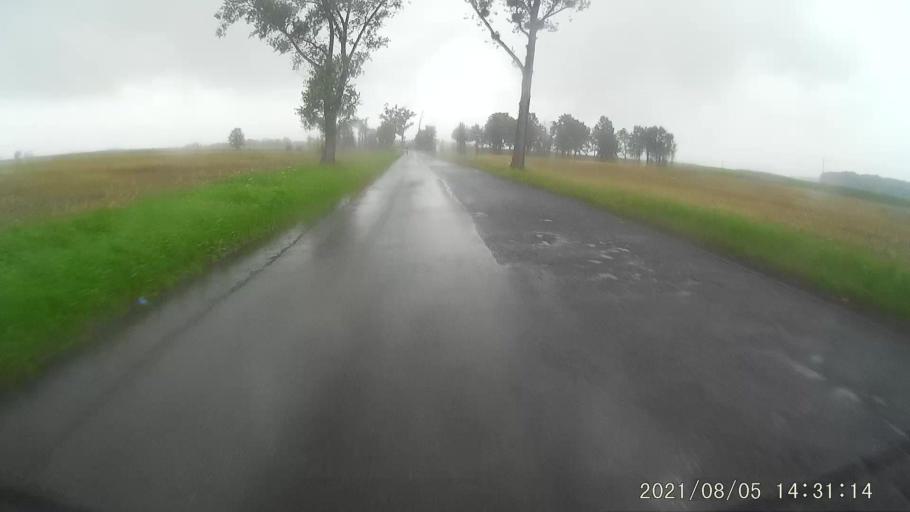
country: PL
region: Opole Voivodeship
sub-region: Powiat nyski
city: Korfantow
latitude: 50.4767
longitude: 17.5581
